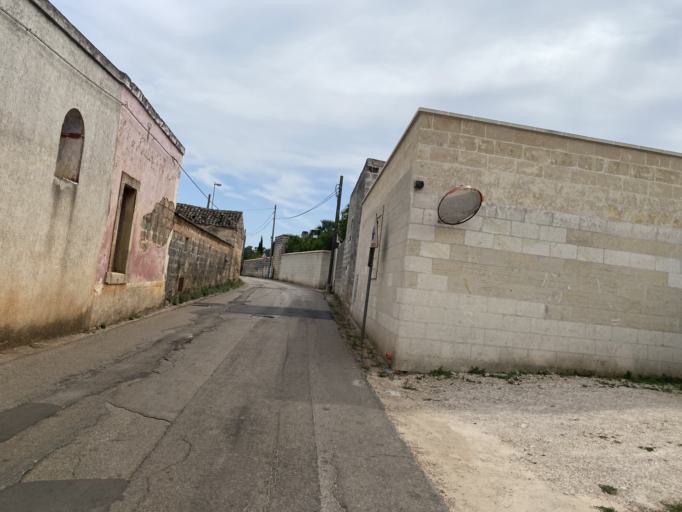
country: IT
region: Apulia
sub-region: Provincia di Lecce
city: Giuggianello
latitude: 40.0907
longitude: 18.3699
